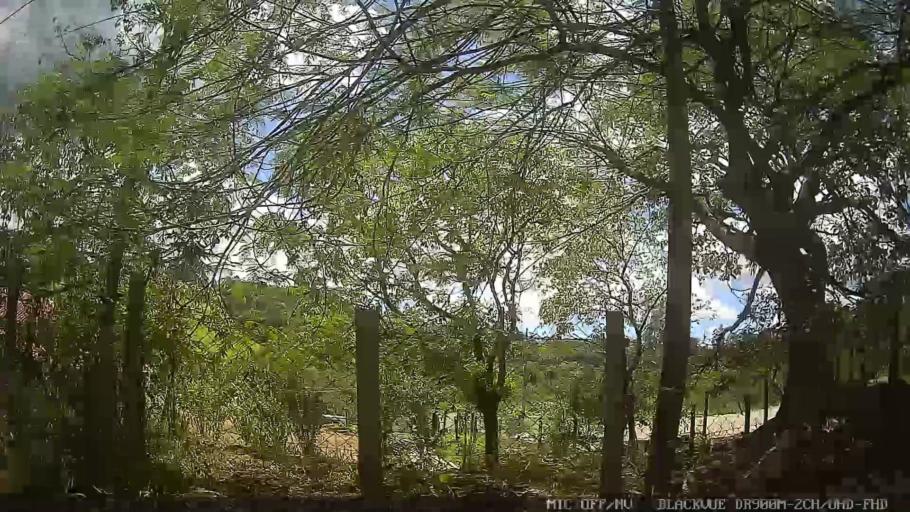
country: BR
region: Sao Paulo
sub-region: Piracaia
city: Piracaia
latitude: -23.0041
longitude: -46.4501
